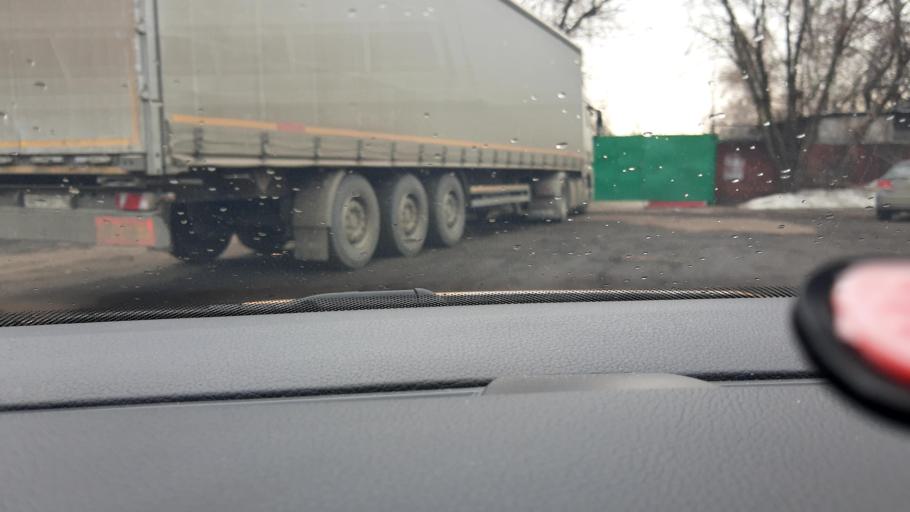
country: RU
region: Moscow
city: Sokol'niki
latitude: 55.7968
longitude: 37.6528
